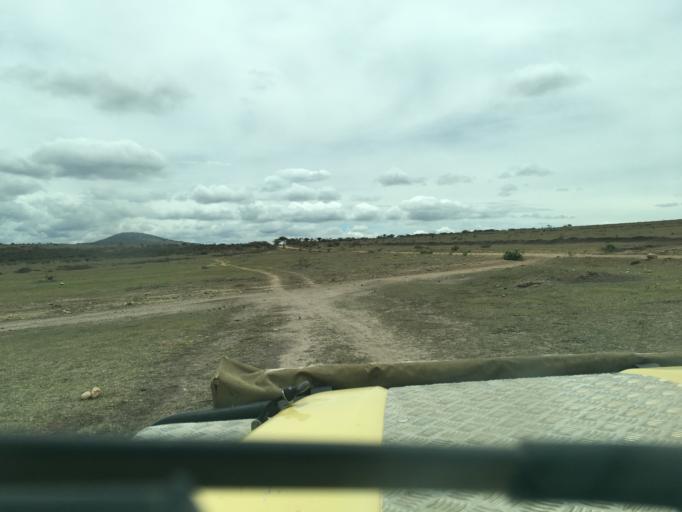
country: KE
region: Kajiado
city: Magadi
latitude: -2.1362
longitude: 35.5681
